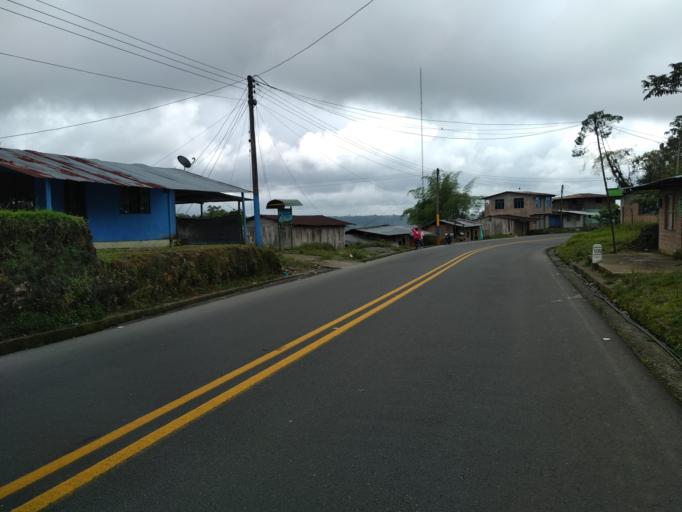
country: CO
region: Narino
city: Ricaurte
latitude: 1.3618
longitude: -78.1832
